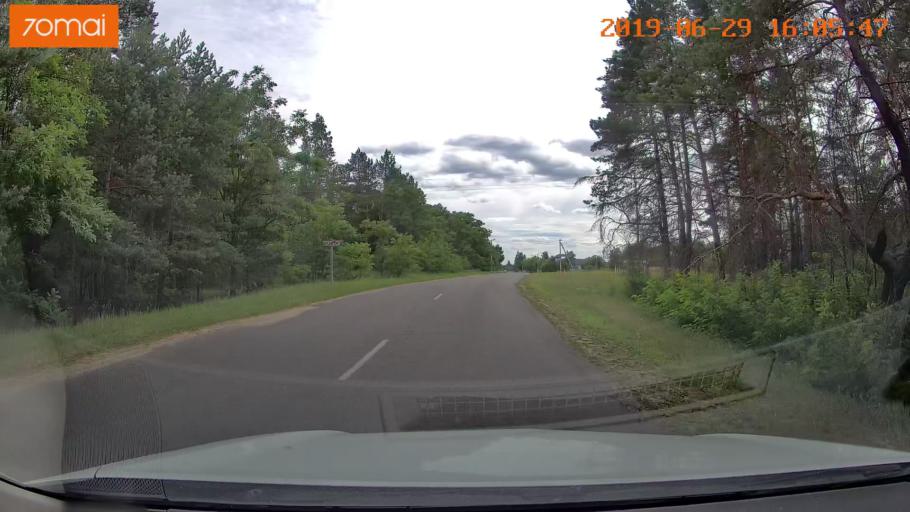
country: BY
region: Brest
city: Luninyets
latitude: 52.2139
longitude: 27.0173
